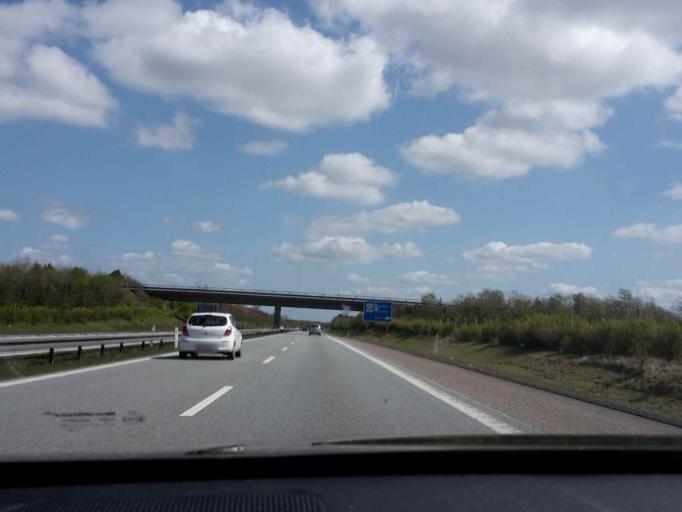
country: DK
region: South Denmark
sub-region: Vejen Kommune
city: Vejen
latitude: 55.4949
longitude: 9.1105
